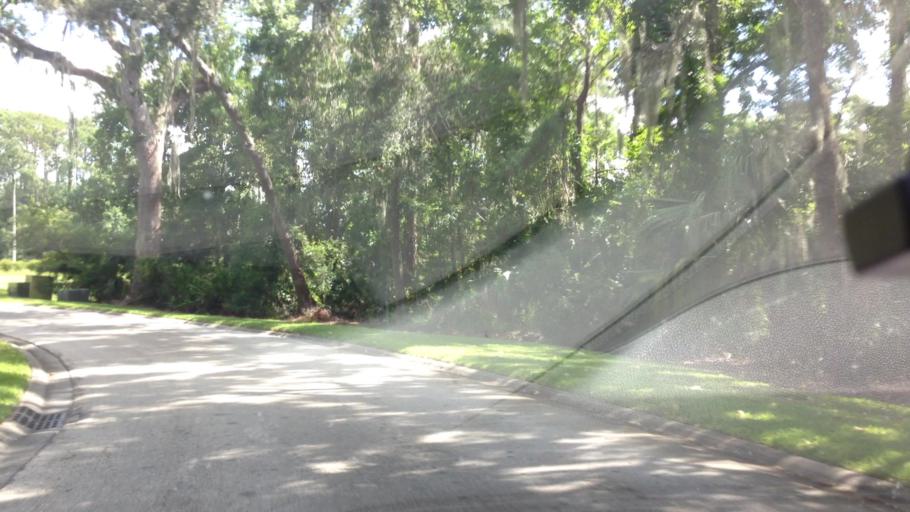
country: US
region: Florida
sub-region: Saint Johns County
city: Ponte Vedra Beach
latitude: 30.2550
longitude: -81.4002
